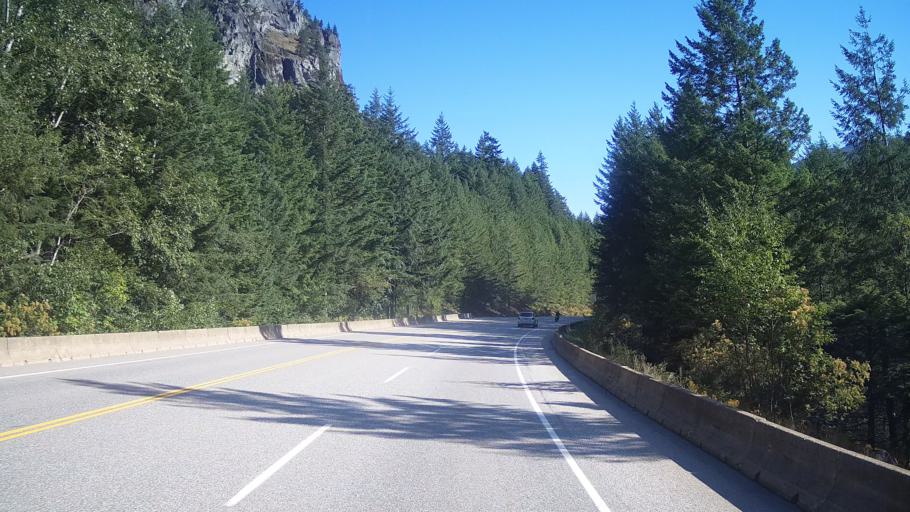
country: CA
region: British Columbia
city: Hope
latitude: 49.6452
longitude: -121.4106
